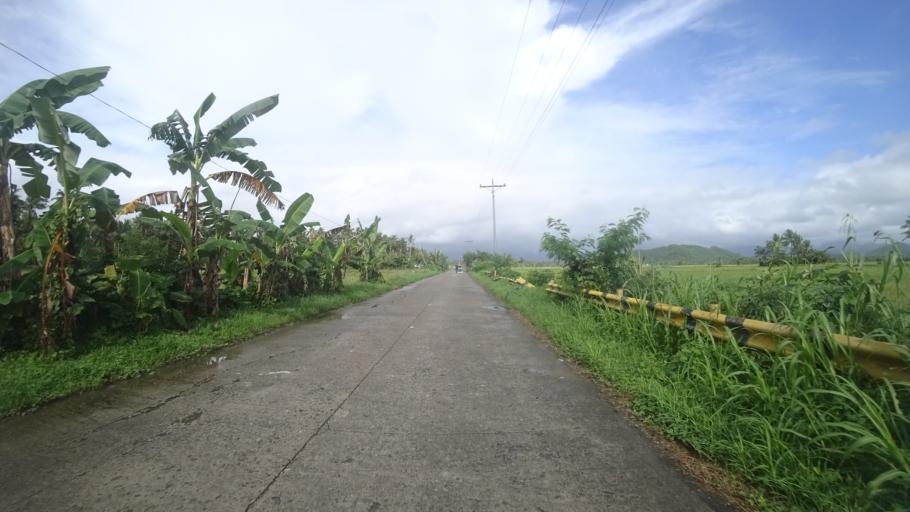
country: PH
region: Eastern Visayas
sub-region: Province of Leyte
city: MacArthur
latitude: 10.8190
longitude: 124.9827
